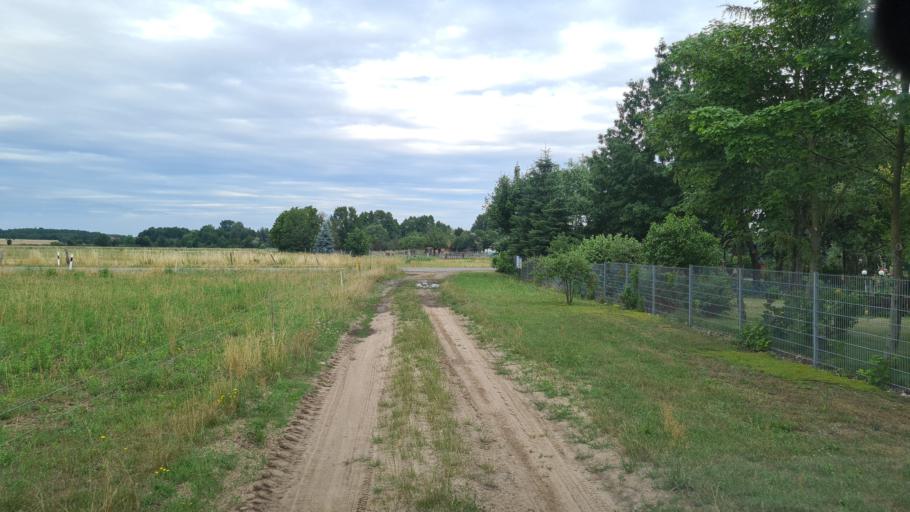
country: DE
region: Brandenburg
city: Crinitz
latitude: 51.7202
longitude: 13.8344
